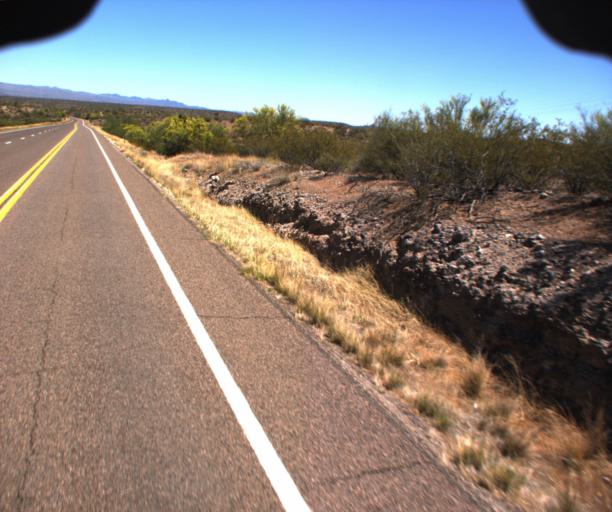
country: US
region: Arizona
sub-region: Maricopa County
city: Wickenburg
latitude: 33.9498
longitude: -112.8704
